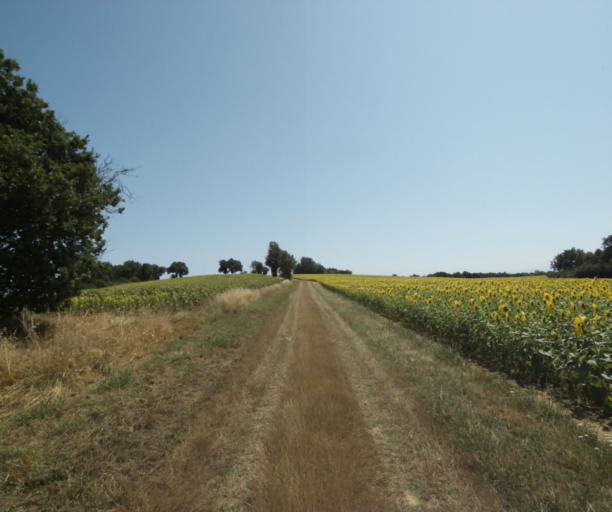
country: FR
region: Midi-Pyrenees
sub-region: Departement de la Haute-Garonne
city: Saint-Felix-Lauragais
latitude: 43.4500
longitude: 1.8579
